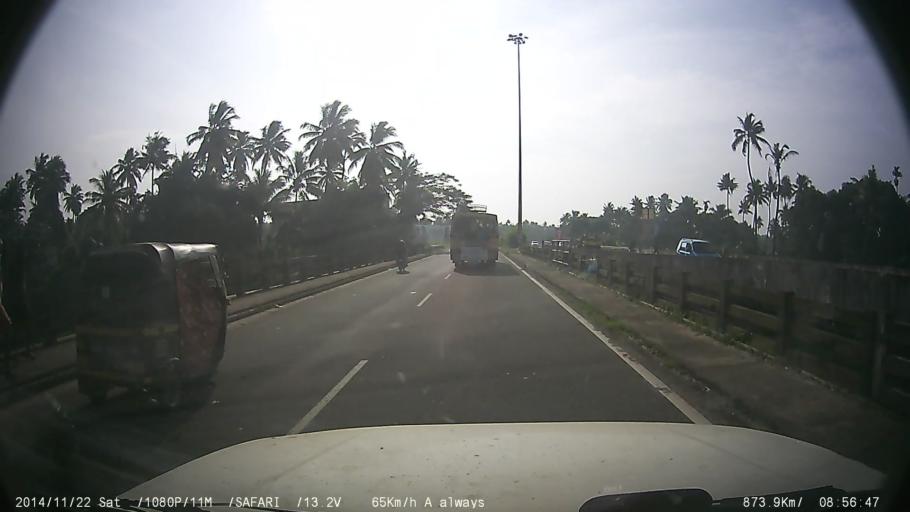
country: IN
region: Kerala
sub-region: Thrissur District
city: Irinjalakuda
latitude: 10.4124
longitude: 76.2715
